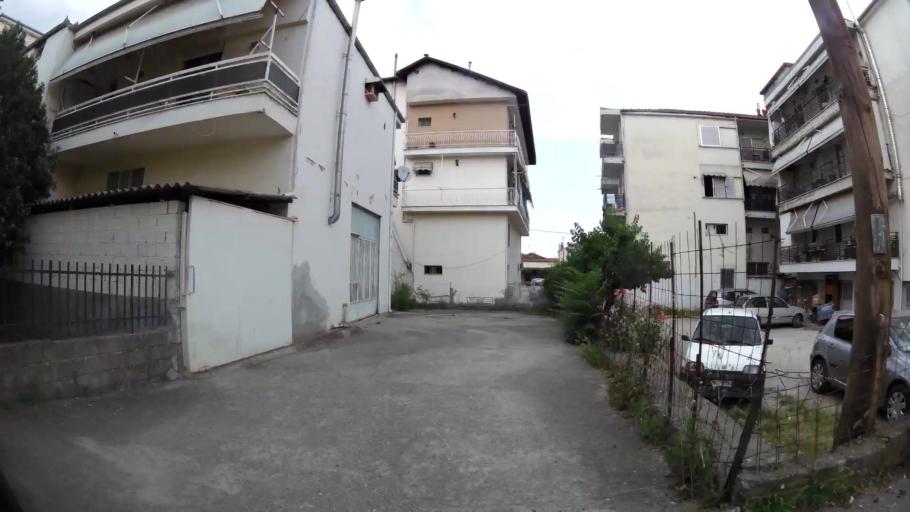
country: GR
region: Central Macedonia
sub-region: Nomos Imathias
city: Veroia
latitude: 40.5322
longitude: 22.2068
